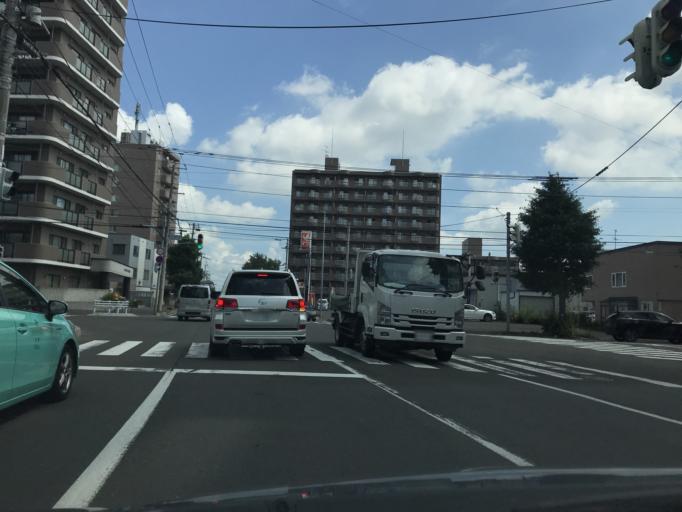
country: JP
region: Hokkaido
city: Sapporo
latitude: 43.0591
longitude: 141.3808
